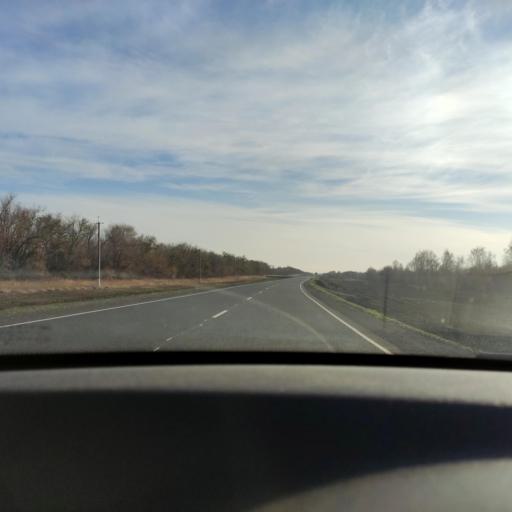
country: RU
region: Samara
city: Krasnoarmeyskoye
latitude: 52.8328
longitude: 50.0062
